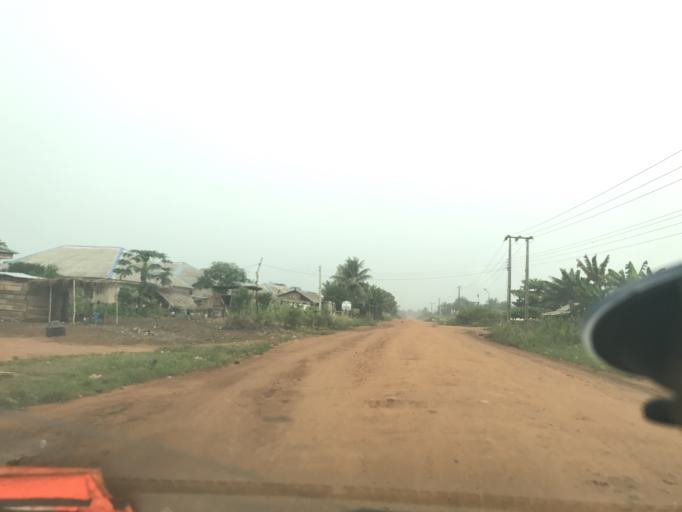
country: NG
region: Ogun
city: Ado Odo
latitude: 6.5370
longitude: 2.9500
